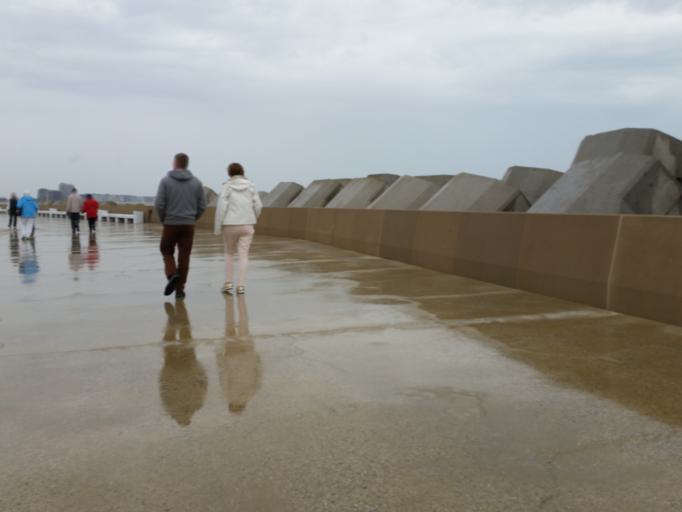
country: BE
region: Flanders
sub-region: Provincie West-Vlaanderen
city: Ostend
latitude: 51.2404
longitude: 2.9156
